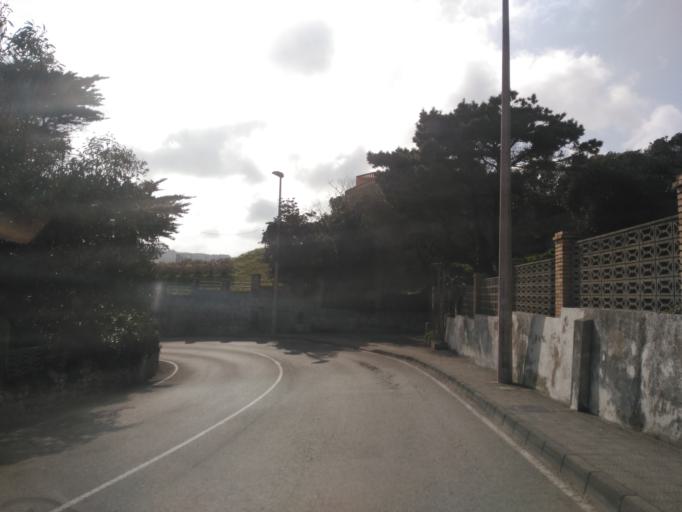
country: ES
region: Cantabria
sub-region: Provincia de Cantabria
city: Suances
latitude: 43.4360
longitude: -4.0460
